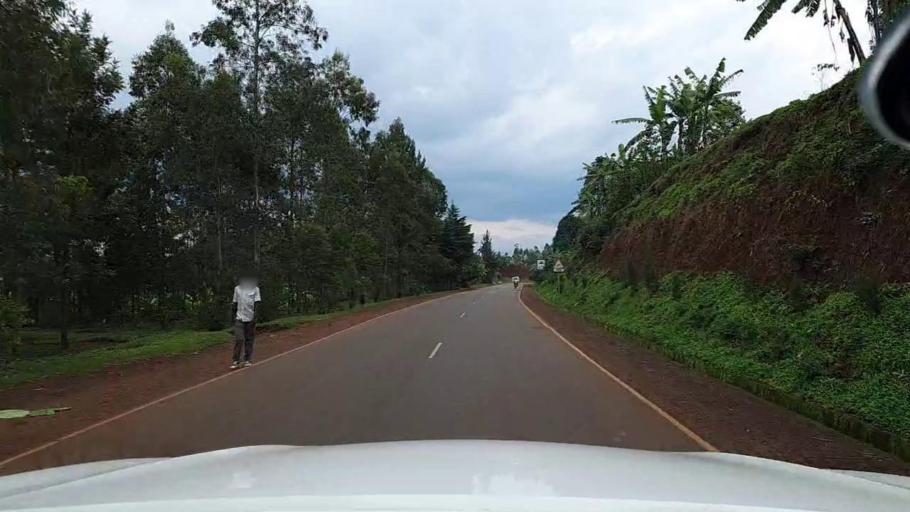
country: RW
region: Western Province
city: Cyangugu
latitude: -2.6457
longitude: 28.9606
